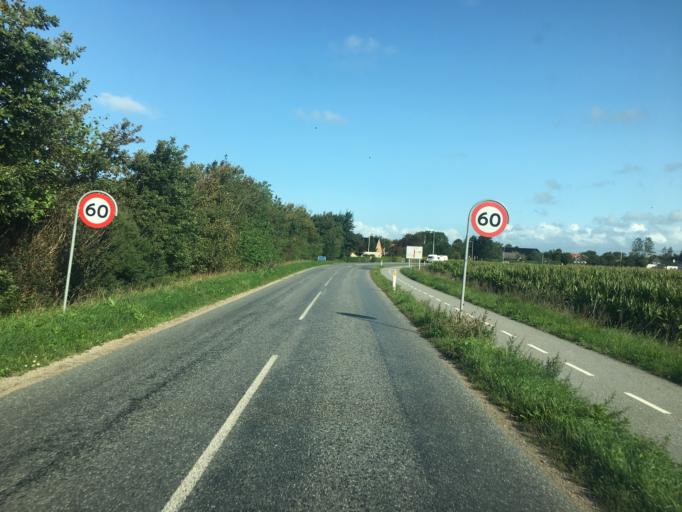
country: DK
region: South Denmark
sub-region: Tonder Kommune
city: Sherrebek
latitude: 55.1479
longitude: 8.7557
